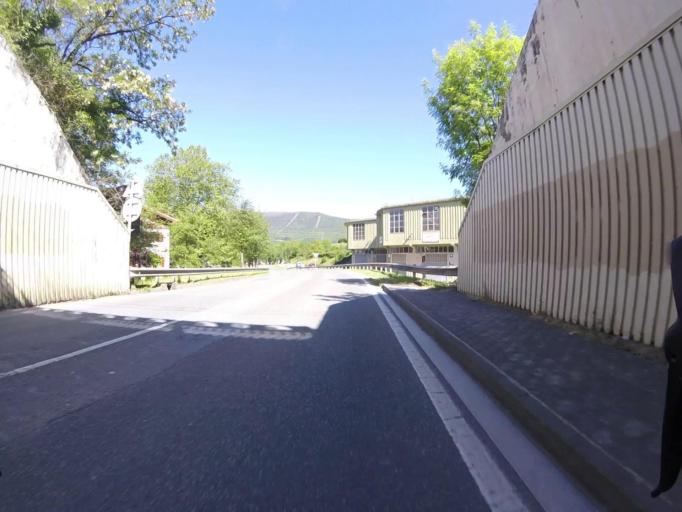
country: ES
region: Basque Country
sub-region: Provincia de Guipuzcoa
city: Irun
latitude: 43.3276
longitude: -1.8222
